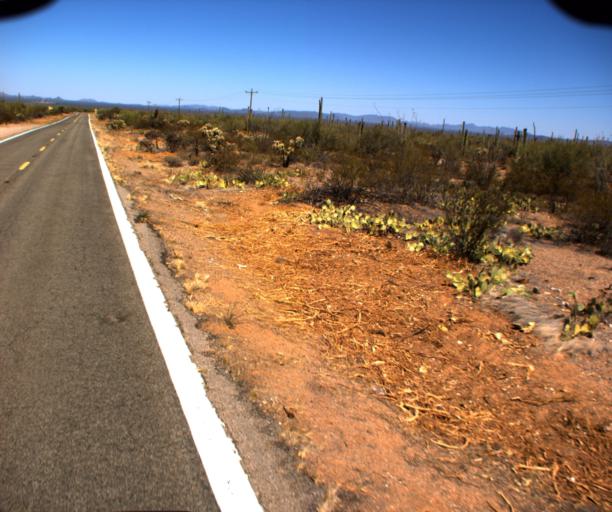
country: US
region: Arizona
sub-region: Pima County
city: Sells
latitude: 32.1773
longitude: -112.2674
